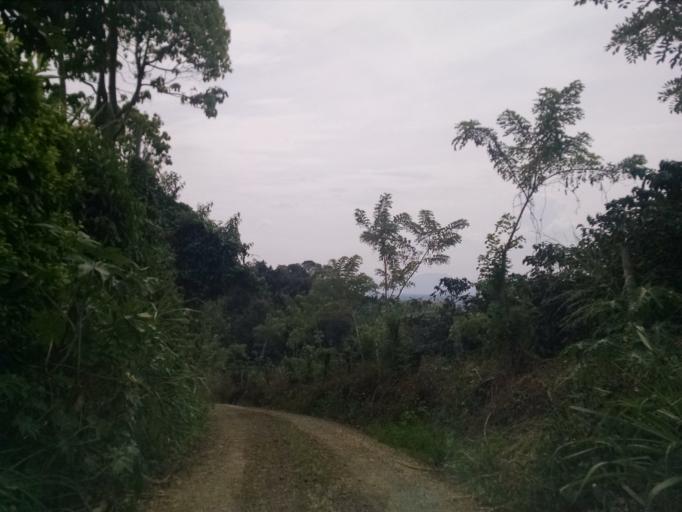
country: CO
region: Valle del Cauca
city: Ulloa
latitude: 4.7199
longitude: -75.7374
